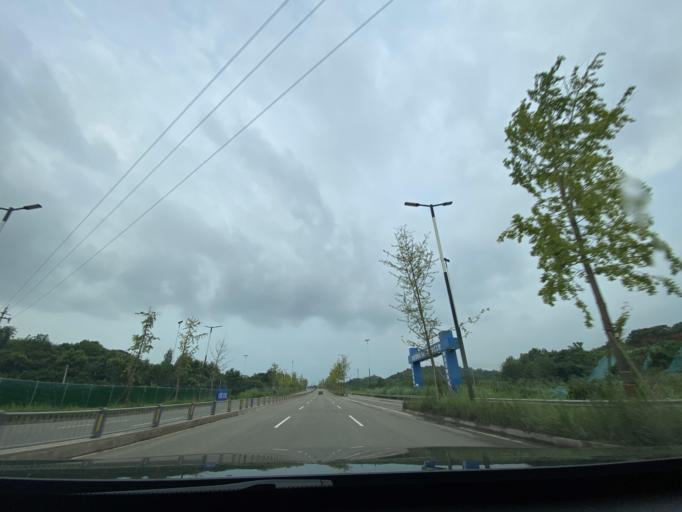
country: CN
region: Sichuan
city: Jiancheng
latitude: 30.4902
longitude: 104.4711
